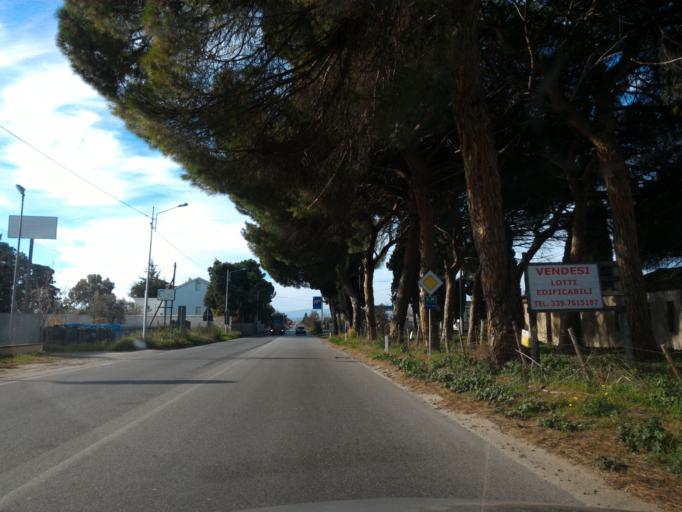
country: IT
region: Calabria
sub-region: Provincia di Catanzaro
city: Sellia Marina
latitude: 38.9049
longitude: 16.7616
